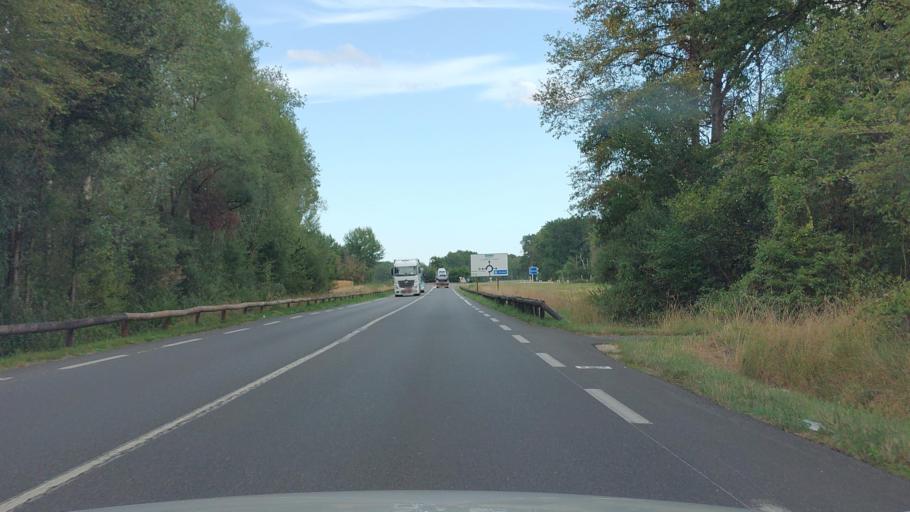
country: FR
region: Ile-de-France
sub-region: Departement de Seine-et-Marne
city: Le Chatelet-en-Brie
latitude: 48.5443
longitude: 2.7932
